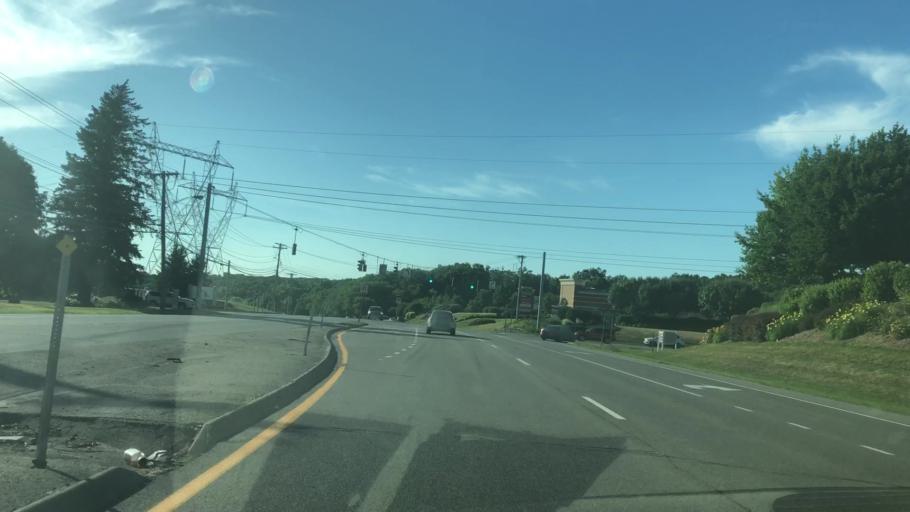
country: US
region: New York
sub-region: Ontario County
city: Victor
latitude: 43.0314
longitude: -77.4408
